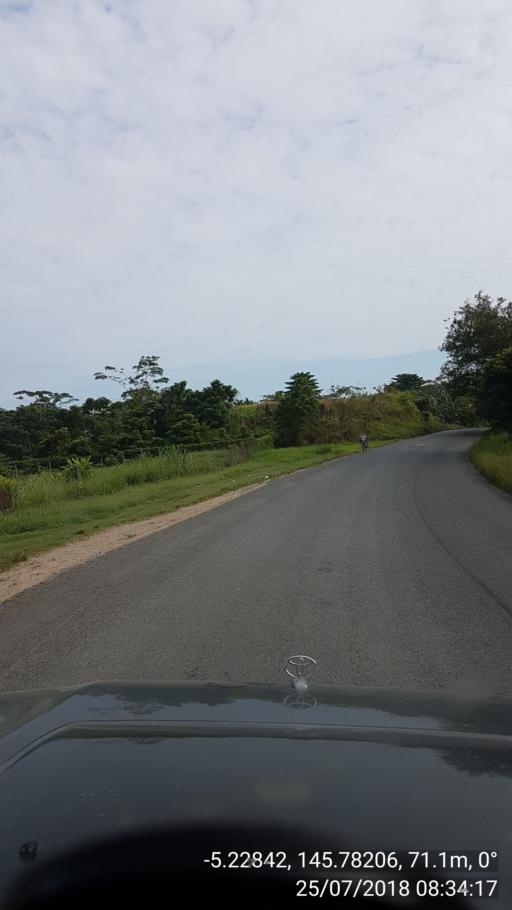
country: PG
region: Madang
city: Madang
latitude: -5.2284
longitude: 145.7824
